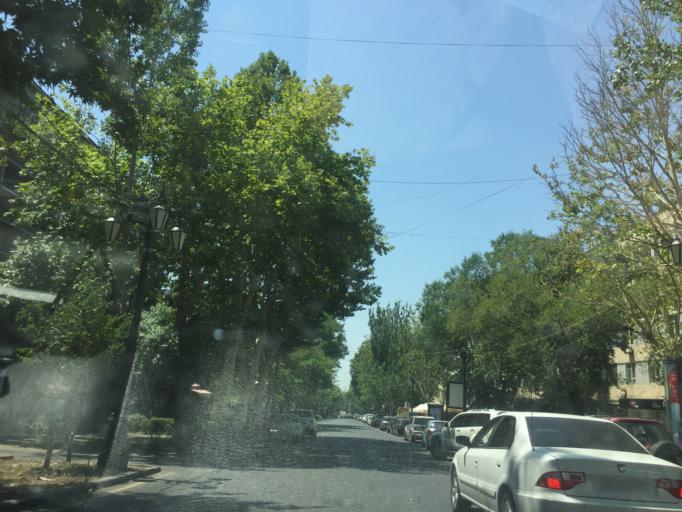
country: AM
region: Yerevan
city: Yerevan
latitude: 40.1856
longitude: 44.5211
